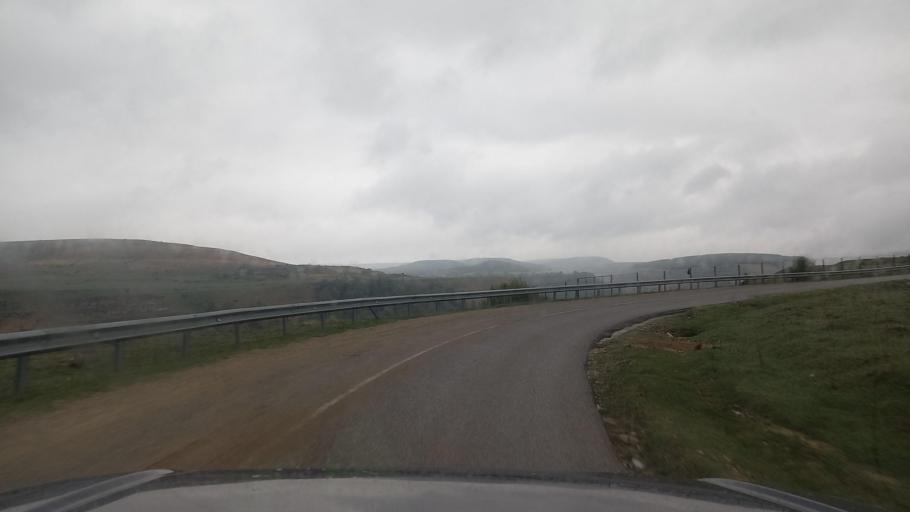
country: RU
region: Stavropol'skiy
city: Nezhinskiy
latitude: 43.8643
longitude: 42.6623
